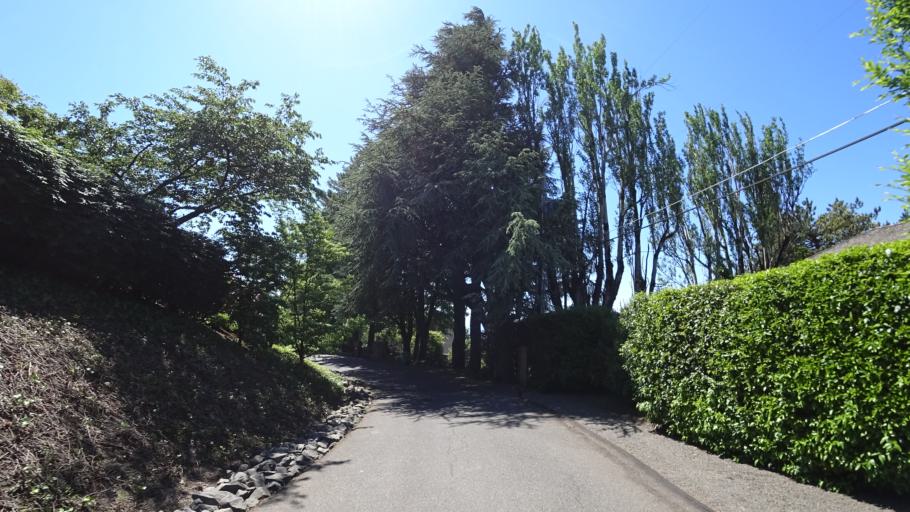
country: US
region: Oregon
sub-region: Washington County
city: West Slope
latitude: 45.5032
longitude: -122.7227
